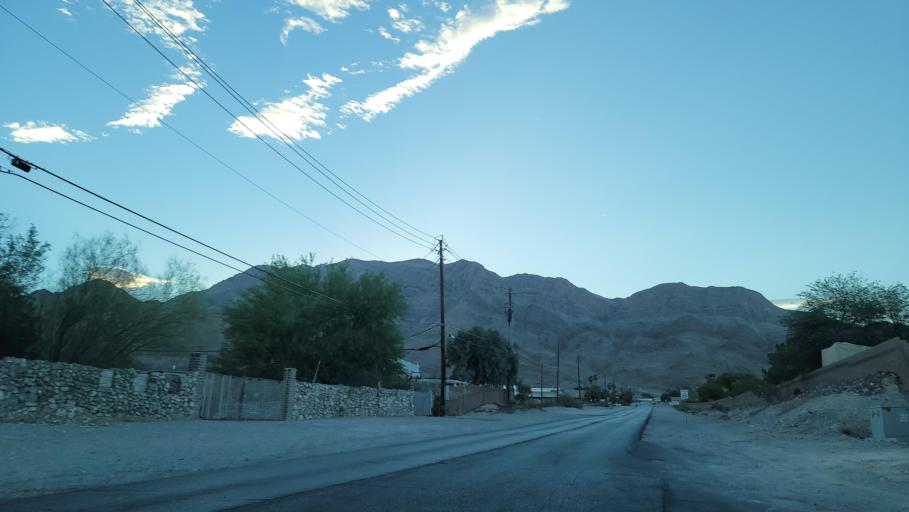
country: US
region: Nevada
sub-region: Clark County
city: Sunrise Manor
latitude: 36.1665
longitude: -115.0257
